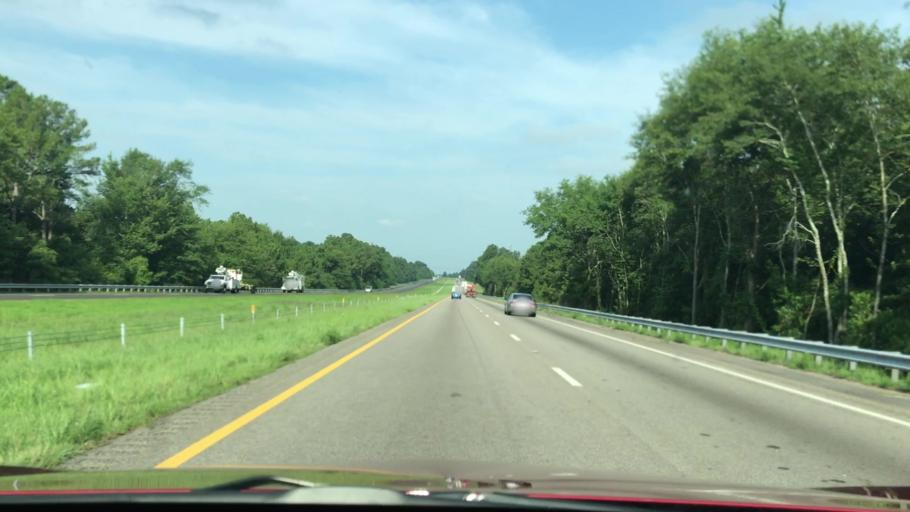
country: US
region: South Carolina
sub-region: Aiken County
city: Graniteville
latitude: 33.6348
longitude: -81.7711
